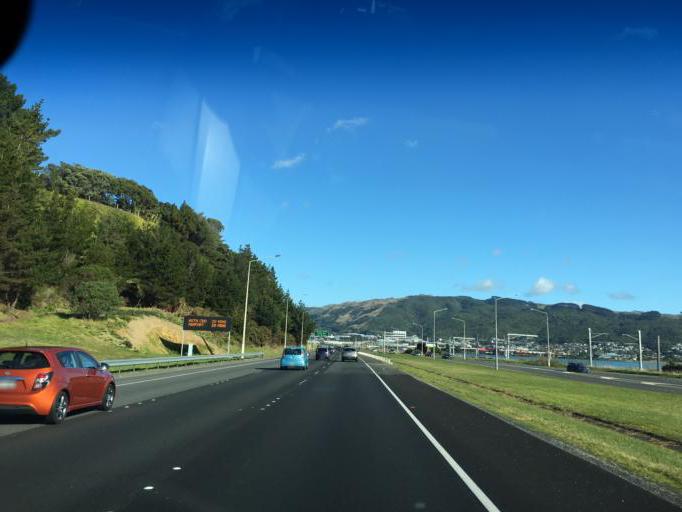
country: NZ
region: Wellington
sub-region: Porirua City
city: Porirua
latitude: -41.1219
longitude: 174.8527
